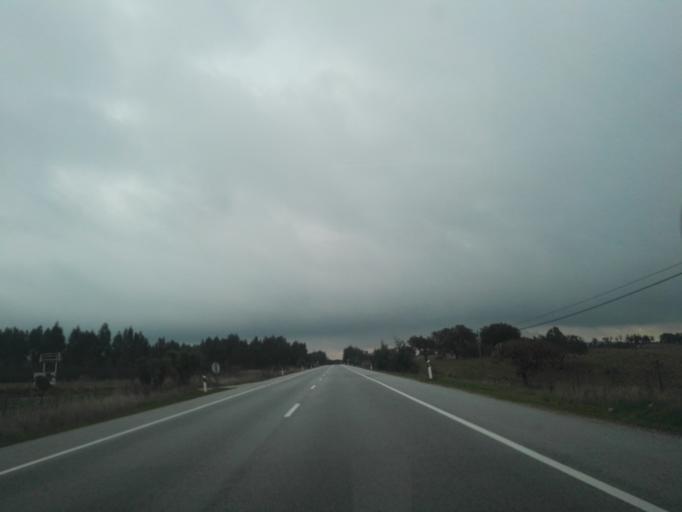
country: PT
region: Portalegre
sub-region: Portalegre
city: Urra
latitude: 39.2315
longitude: -7.3867
